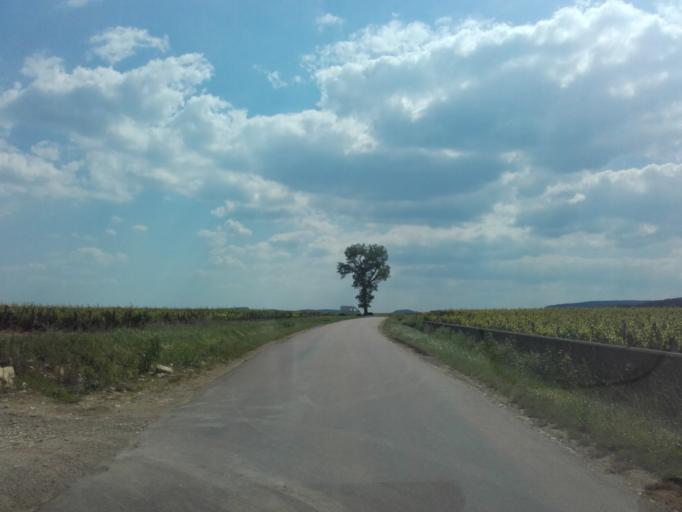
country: FR
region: Bourgogne
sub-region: Departement de la Cote-d'Or
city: Meursault
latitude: 46.9626
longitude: 4.7610
